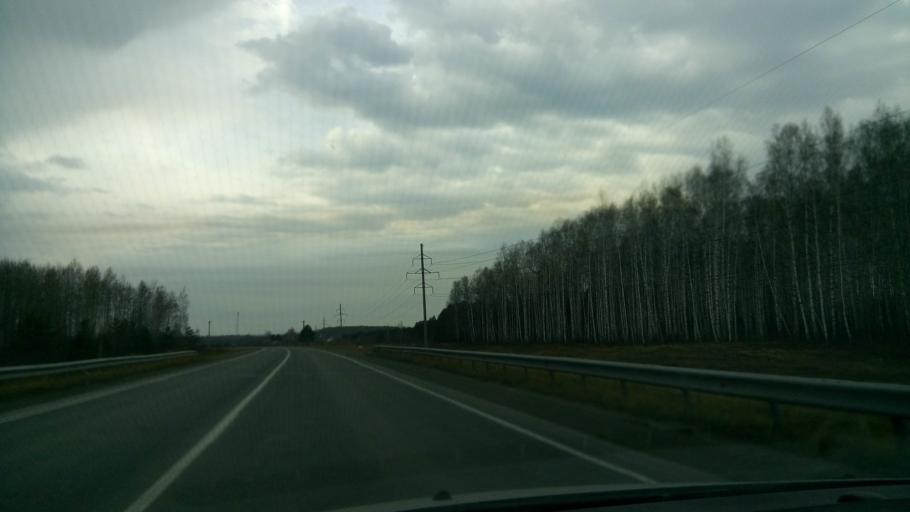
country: RU
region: Sverdlovsk
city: Obukhovskoye
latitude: 56.8584
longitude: 62.6205
